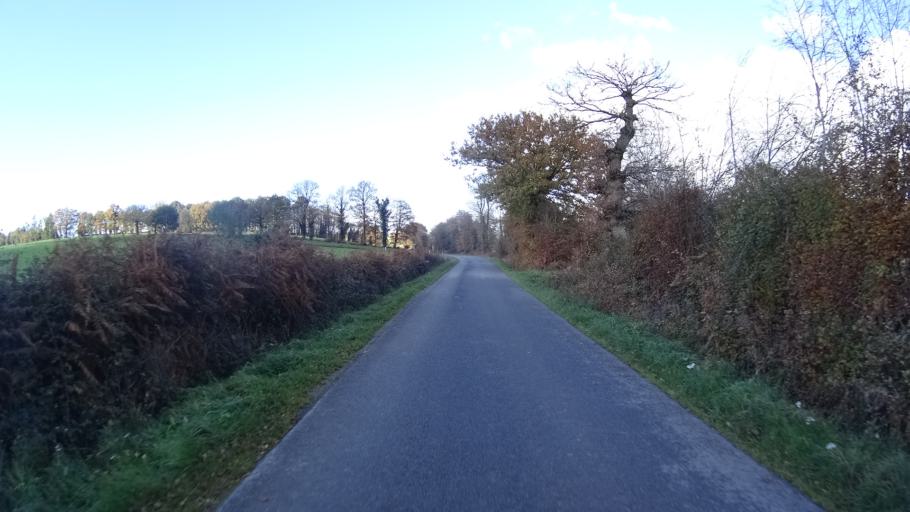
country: FR
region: Brittany
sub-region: Departement du Morbihan
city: Carentoir
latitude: 47.8072
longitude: -2.1753
